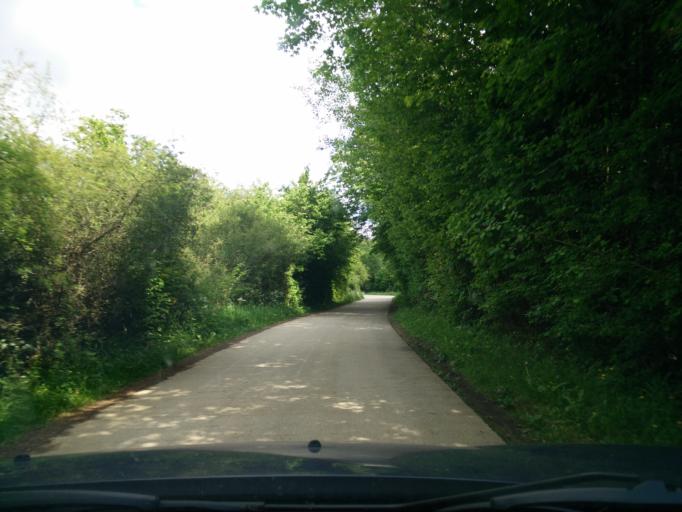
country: FR
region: Champagne-Ardenne
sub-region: Departement des Ardennes
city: Vireux-Molhain
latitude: 50.0873
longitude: 4.6141
